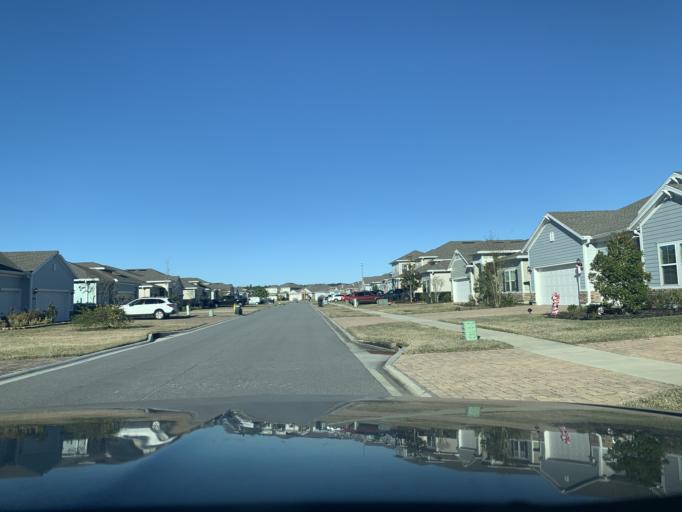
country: US
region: Florida
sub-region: Clay County
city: Green Cove Springs
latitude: 29.9788
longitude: -81.5236
